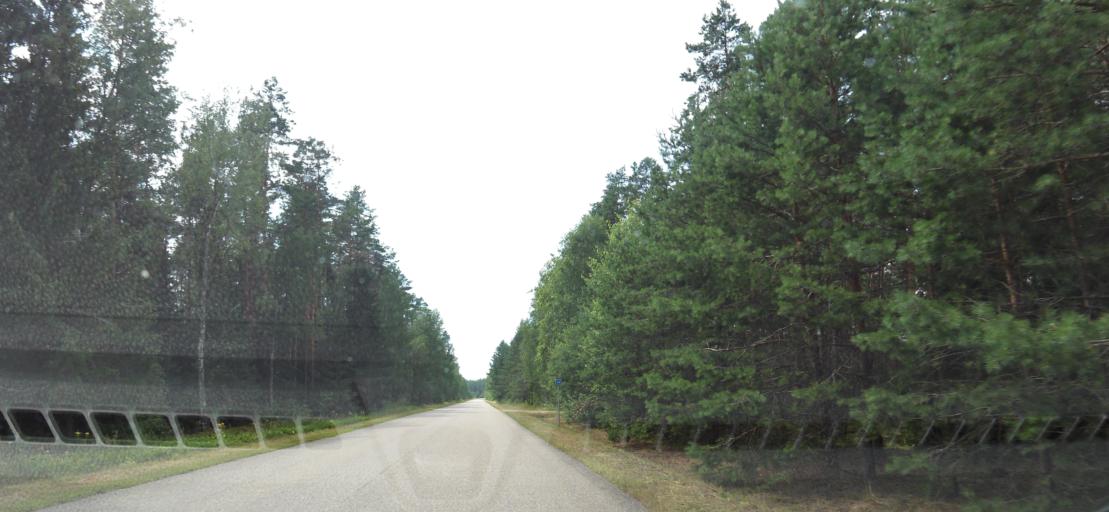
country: LT
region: Alytaus apskritis
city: Druskininkai
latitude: 53.9891
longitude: 24.1448
